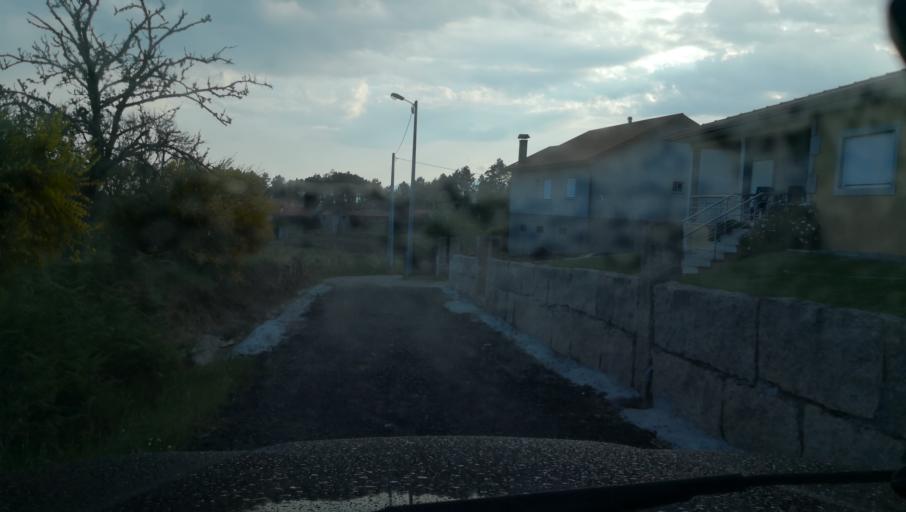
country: PT
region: Vila Real
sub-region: Vila Real
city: Vila Real
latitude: 41.3145
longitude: -7.6800
